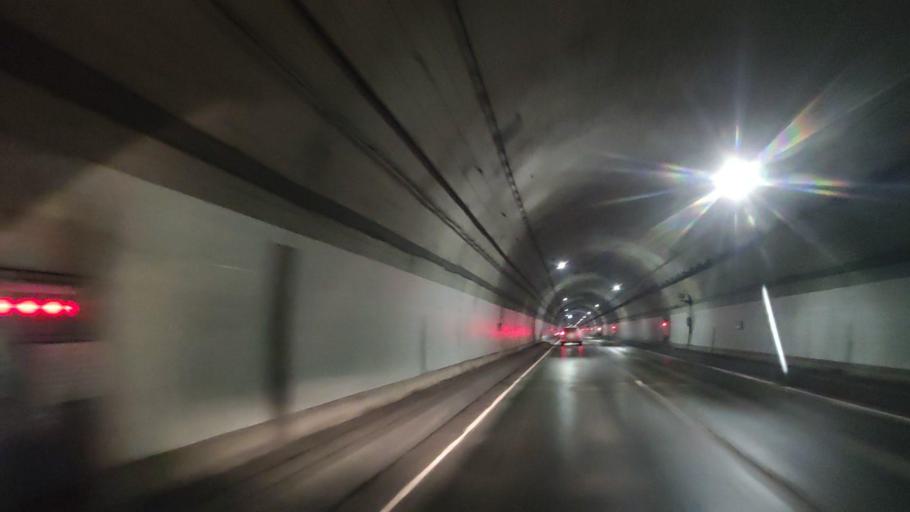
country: JP
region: Hokkaido
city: Rumoi
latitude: 43.7066
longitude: 141.3344
